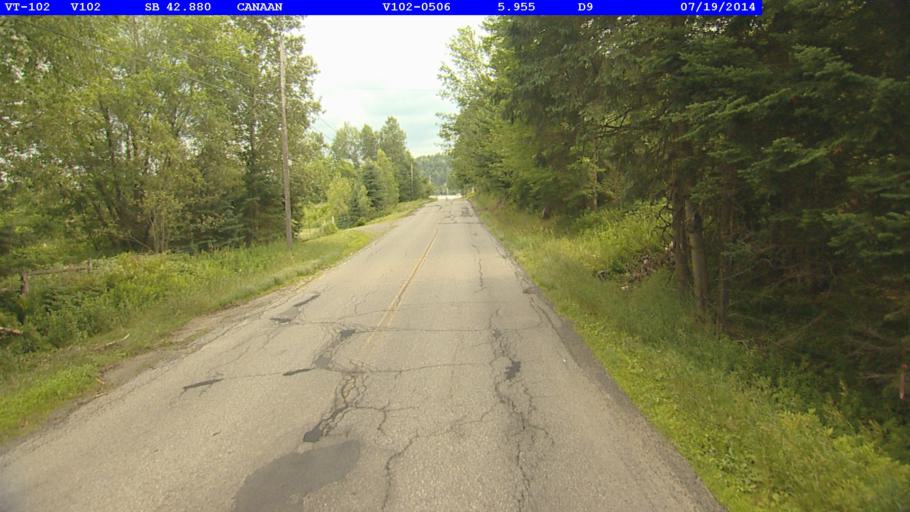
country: US
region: New Hampshire
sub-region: Coos County
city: Colebrook
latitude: 44.9845
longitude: -71.5431
